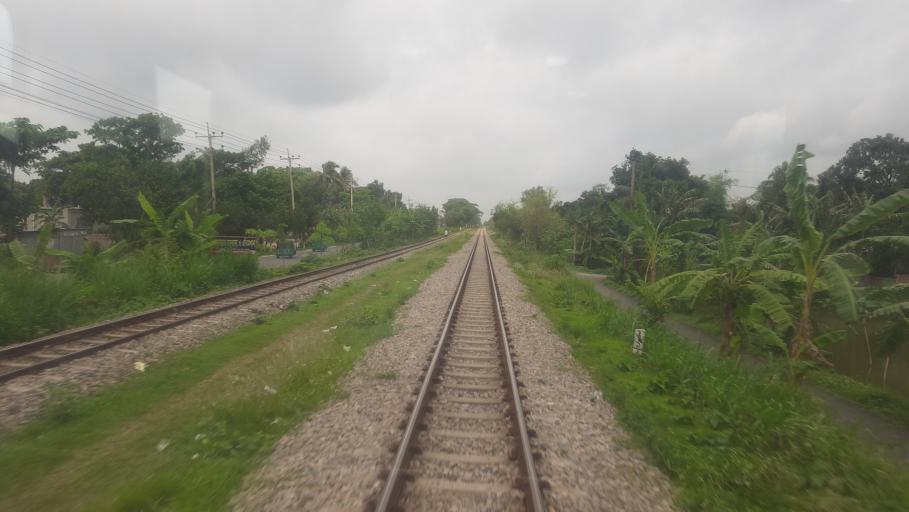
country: BD
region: Dhaka
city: Narsingdi
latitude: 23.9319
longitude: 90.7450
